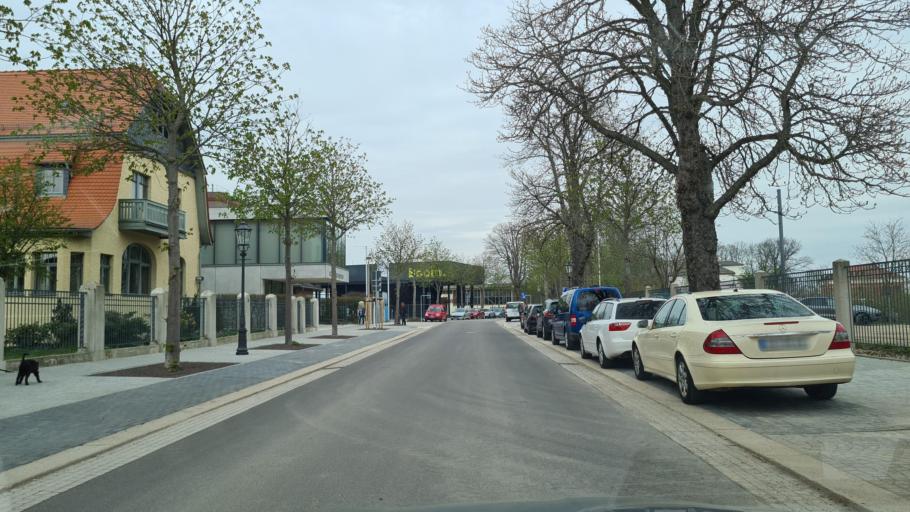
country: DE
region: Saxony
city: Zwickau
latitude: 50.7328
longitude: 12.4847
